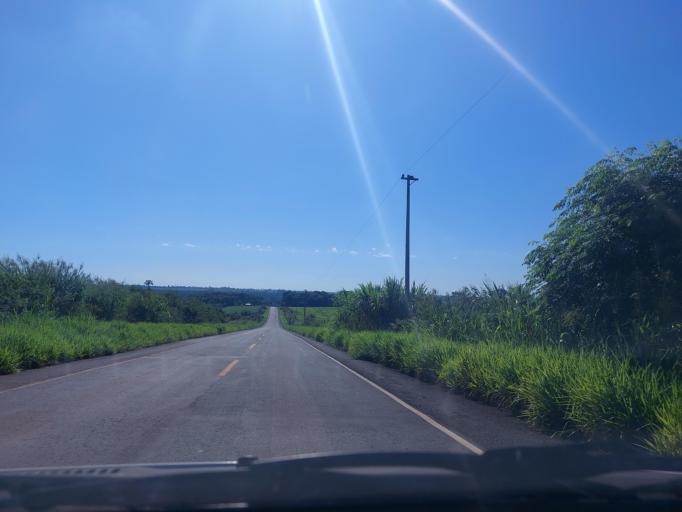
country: PY
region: San Pedro
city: Guayaybi
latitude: -24.3059
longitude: -56.1489
